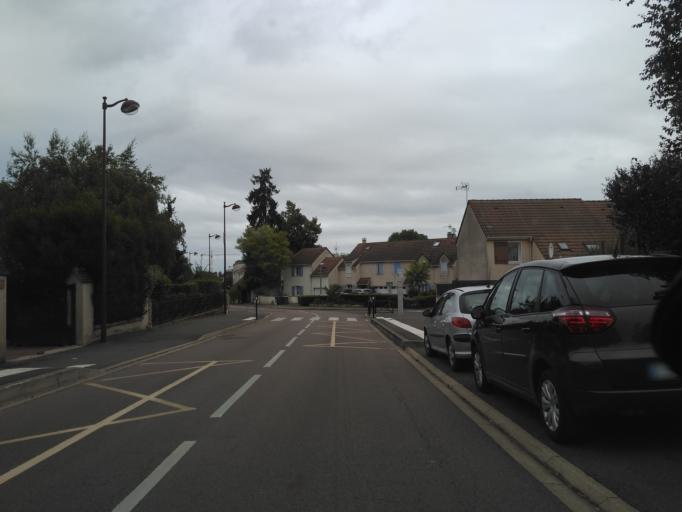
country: FR
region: Ile-de-France
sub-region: Departement de Seine-et-Marne
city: Cesson
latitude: 48.5630
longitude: 2.6131
